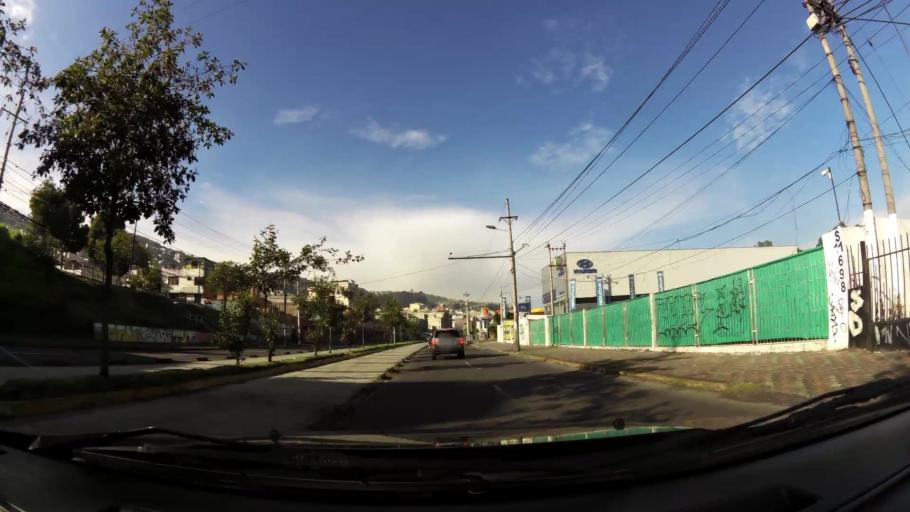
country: EC
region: Pichincha
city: Quito
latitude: -0.2581
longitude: -78.5226
